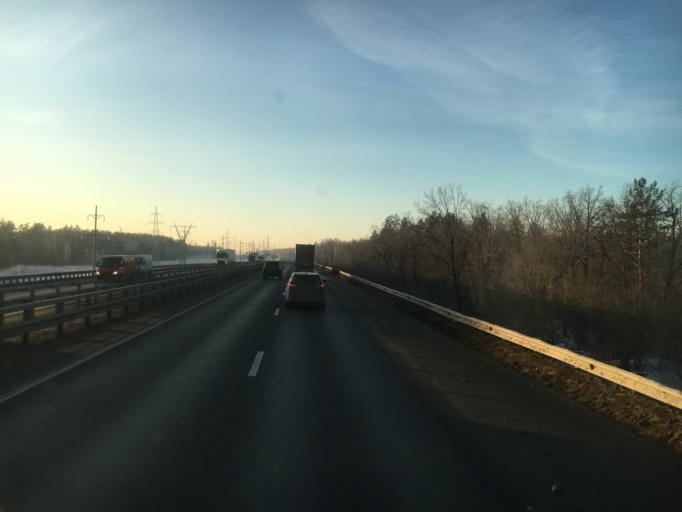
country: RU
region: Samara
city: Pribrezhnyy
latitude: 53.5178
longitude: 49.8342
